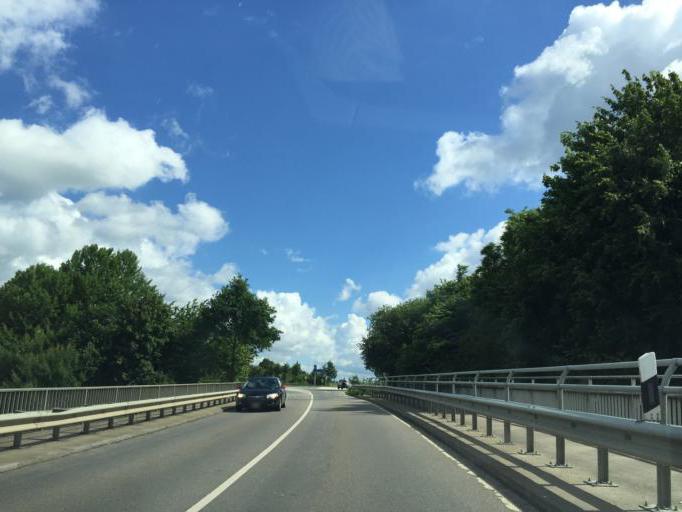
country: DE
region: Schleswig-Holstein
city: Scharbeutz
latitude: 54.0057
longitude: 10.7288
